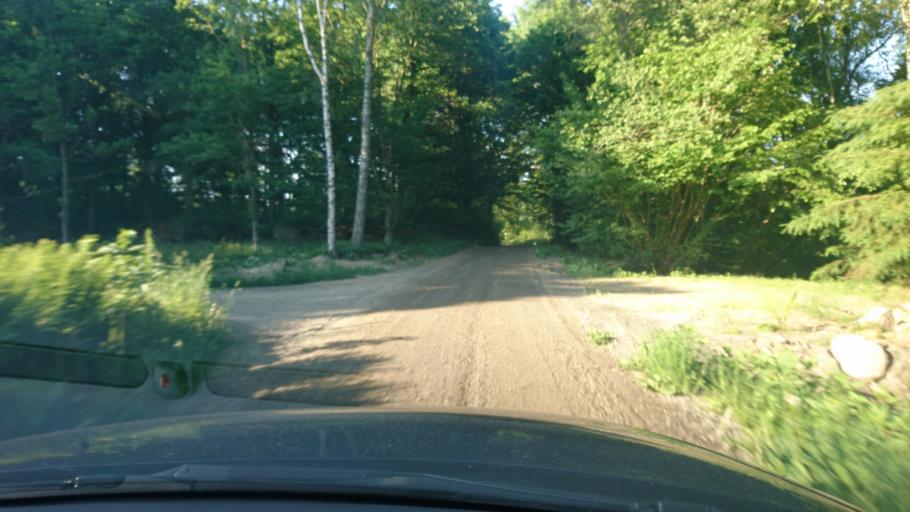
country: SE
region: Skane
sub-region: Osby Kommun
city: Lonsboda
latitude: 56.3757
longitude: 14.3774
